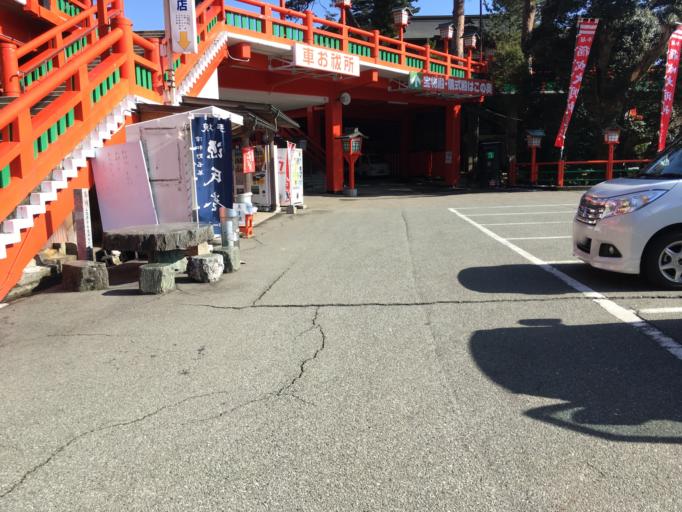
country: JP
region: Shimane
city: Masuda
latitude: 34.4651
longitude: 131.7690
